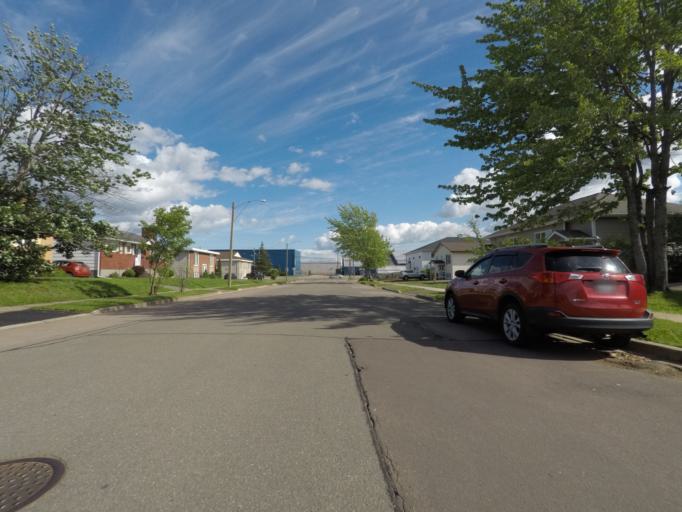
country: CA
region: New Brunswick
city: Moncton
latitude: 46.0959
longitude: -64.8267
